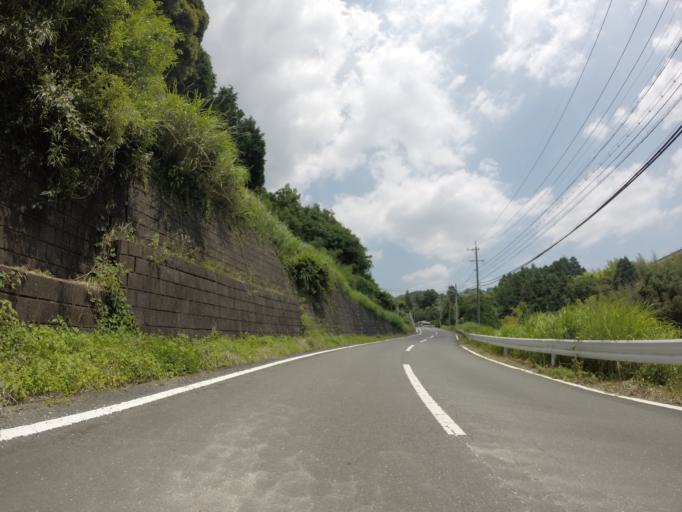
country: JP
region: Shizuoka
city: Kanaya
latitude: 34.8340
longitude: 138.0744
